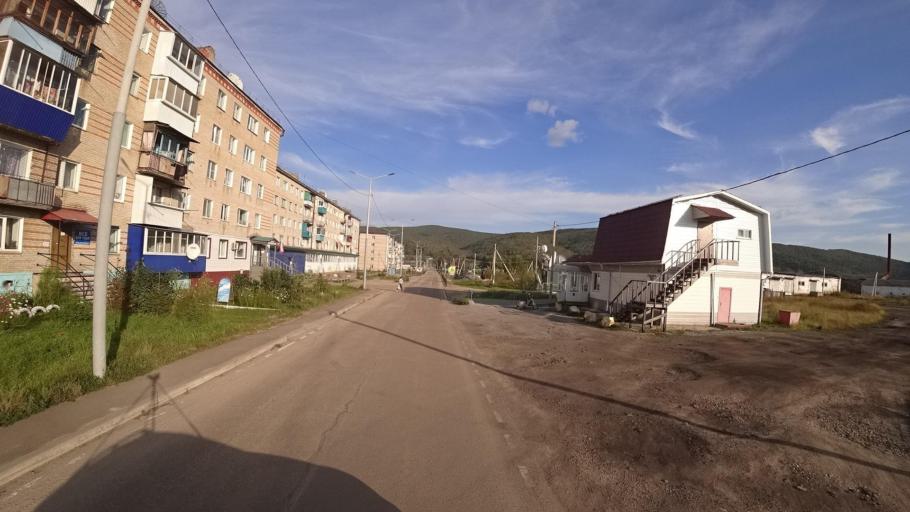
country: RU
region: Jewish Autonomous Oblast
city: Kul'dur
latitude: 49.2022
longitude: 131.6239
